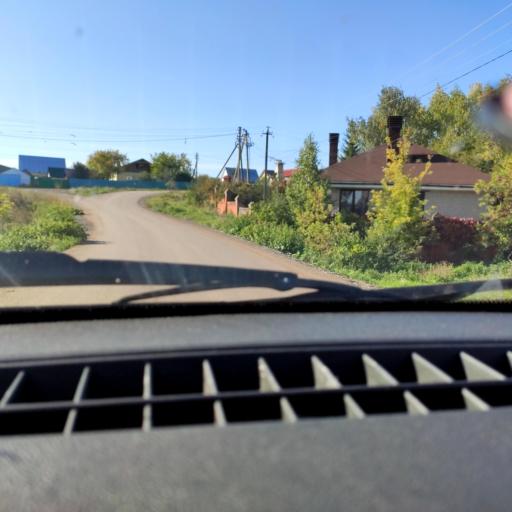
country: RU
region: Bashkortostan
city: Avdon
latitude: 54.6043
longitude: 55.7900
